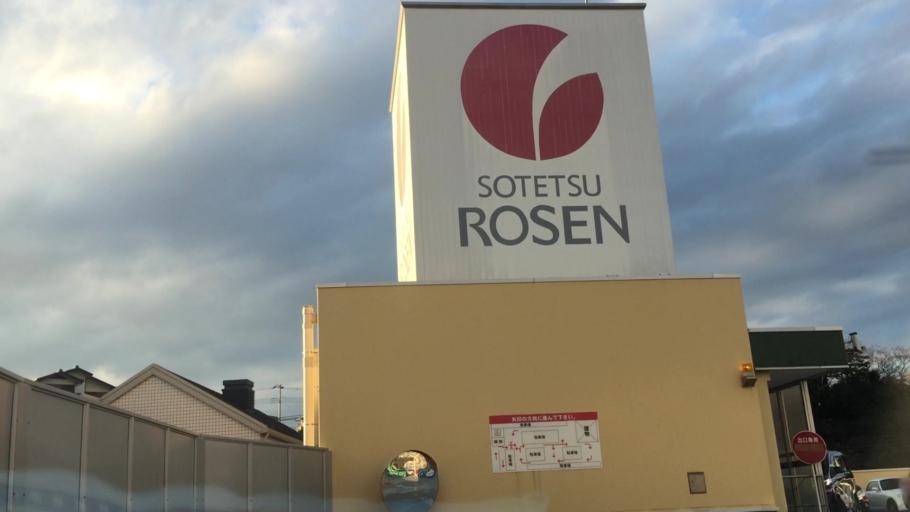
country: JP
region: Kanagawa
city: Zushi
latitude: 35.3402
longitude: 139.6105
